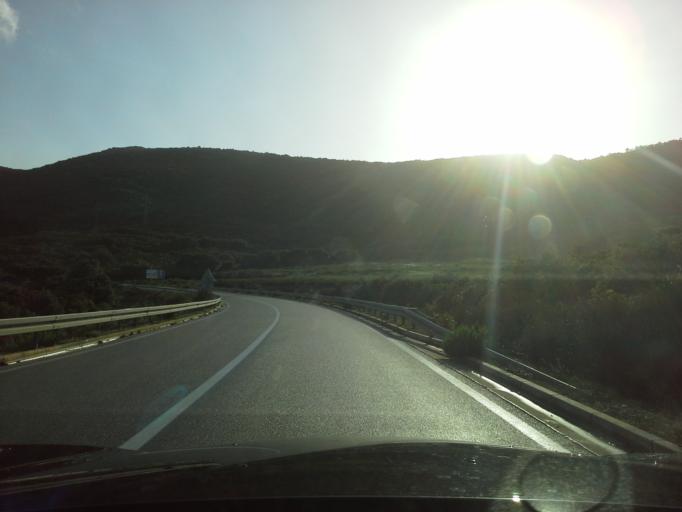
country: HR
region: Primorsko-Goranska
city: Mali Losinj
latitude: 44.6485
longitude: 14.3926
